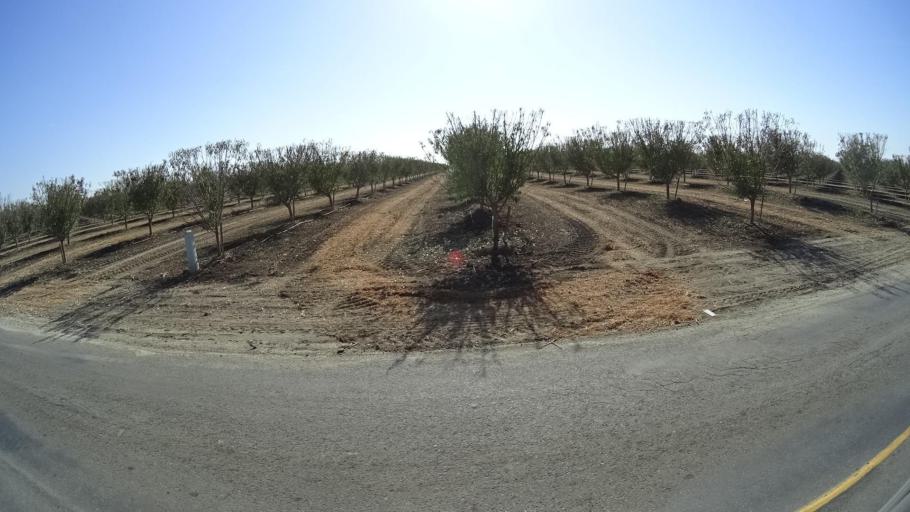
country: US
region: California
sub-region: Kern County
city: McFarland
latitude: 35.7034
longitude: -119.2000
